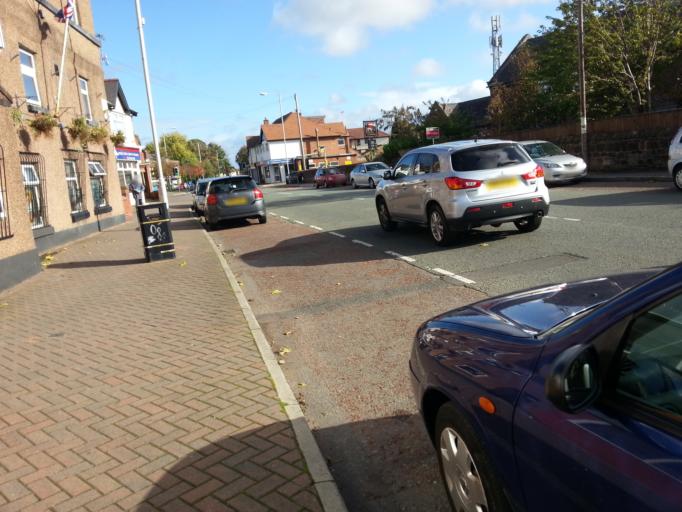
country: GB
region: England
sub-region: Metropolitan Borough of Wirral
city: Heswall
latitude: 53.3521
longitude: -3.1189
